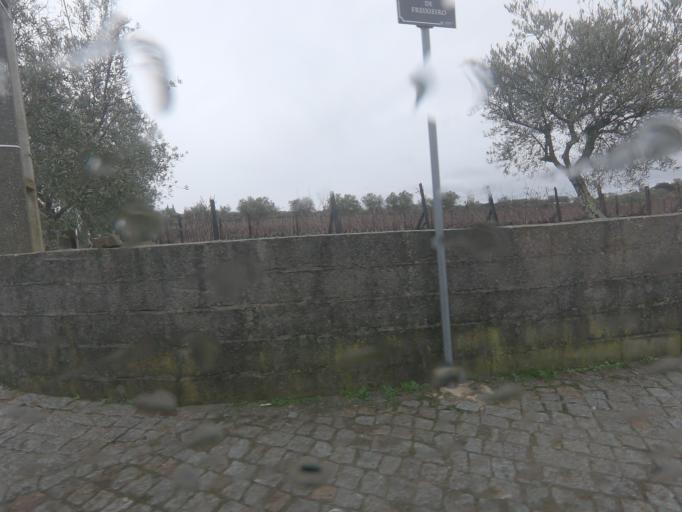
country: PT
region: Vila Real
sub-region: Peso da Regua
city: Peso da Regua
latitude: 41.1791
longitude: -7.7194
